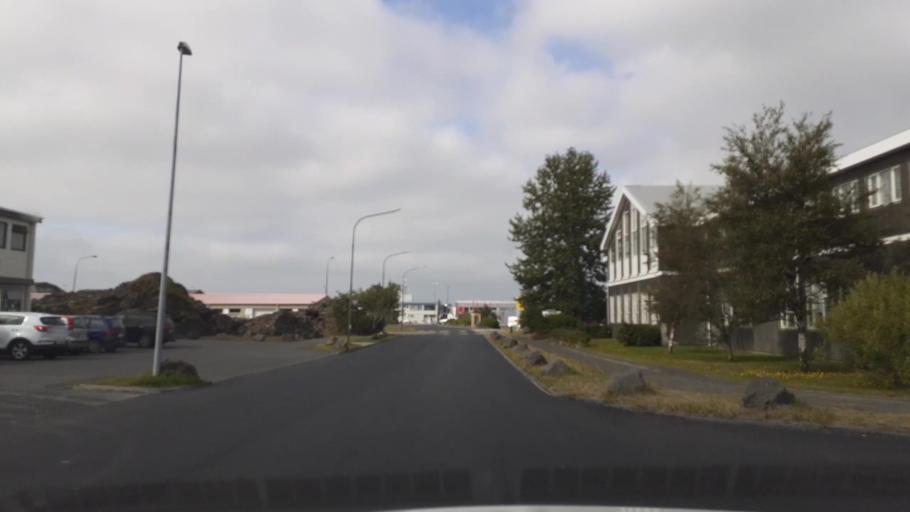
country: IS
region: Capital Region
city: Hafnarfjoerdur
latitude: 64.0816
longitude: -21.9373
